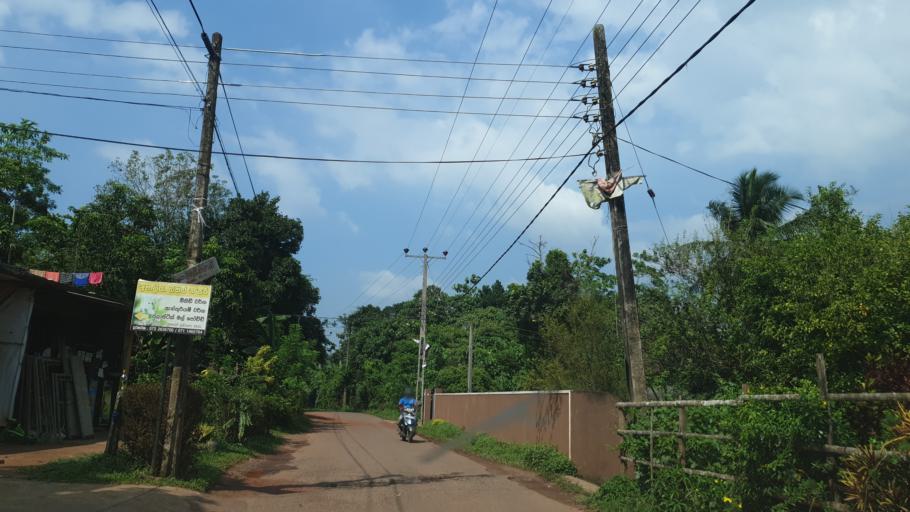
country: LK
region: Western
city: Panadura
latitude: 6.7324
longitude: 79.9529
